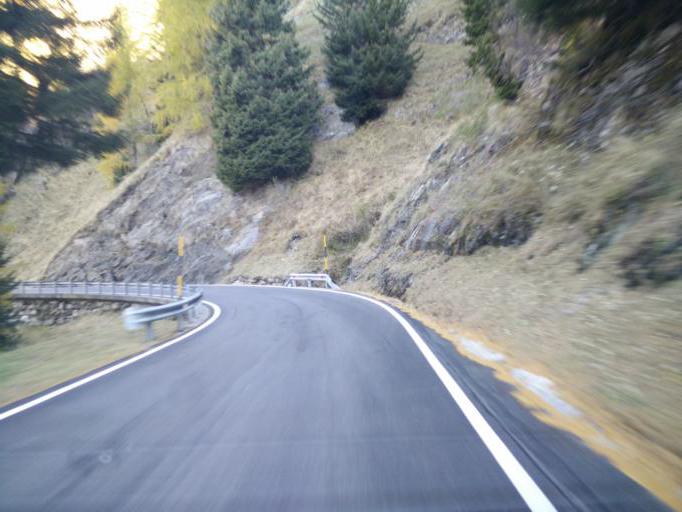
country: IT
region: Trentino-Alto Adige
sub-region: Bolzano
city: Moso in Passiria
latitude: 46.8818
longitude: 11.1508
